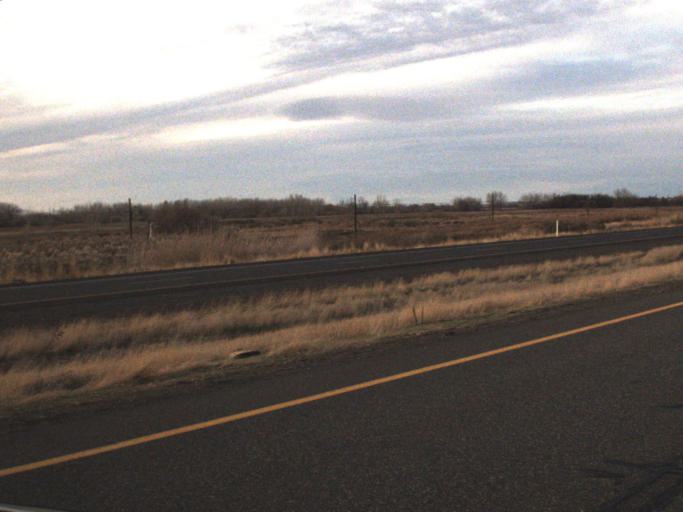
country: US
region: Washington
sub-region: Benton County
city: Finley
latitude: 46.1319
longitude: -118.9331
